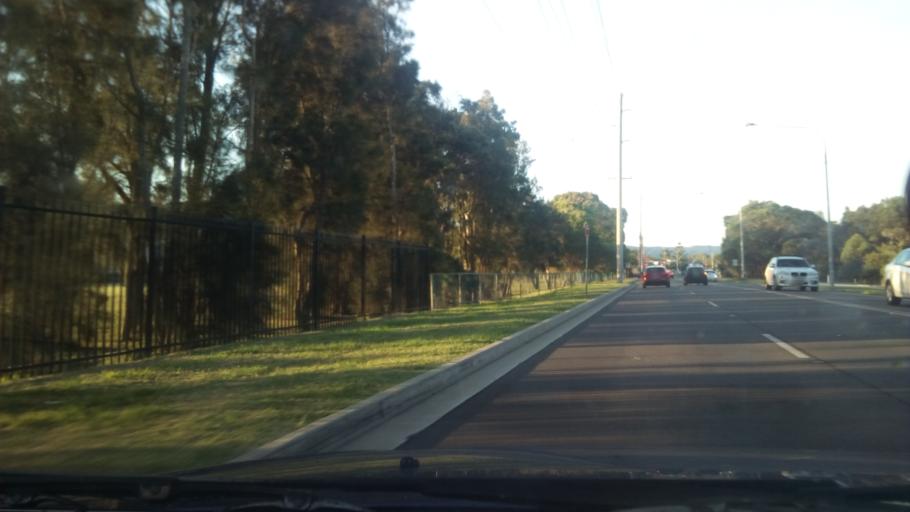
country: AU
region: New South Wales
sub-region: Wollongong
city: Fairy Meadow
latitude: -34.3982
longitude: 150.9008
